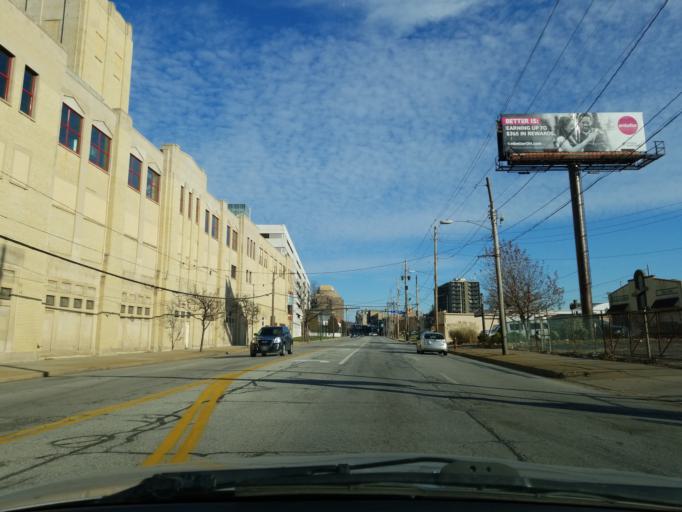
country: US
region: Ohio
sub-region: Cuyahoga County
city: Bratenahl
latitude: 41.5012
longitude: -81.6282
